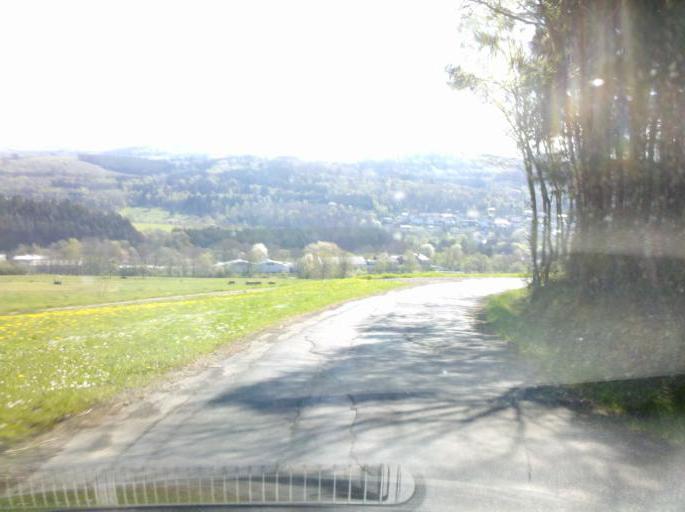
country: DE
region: Hesse
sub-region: Regierungsbezirk Giessen
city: Haiger
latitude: 50.7755
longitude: 8.2000
